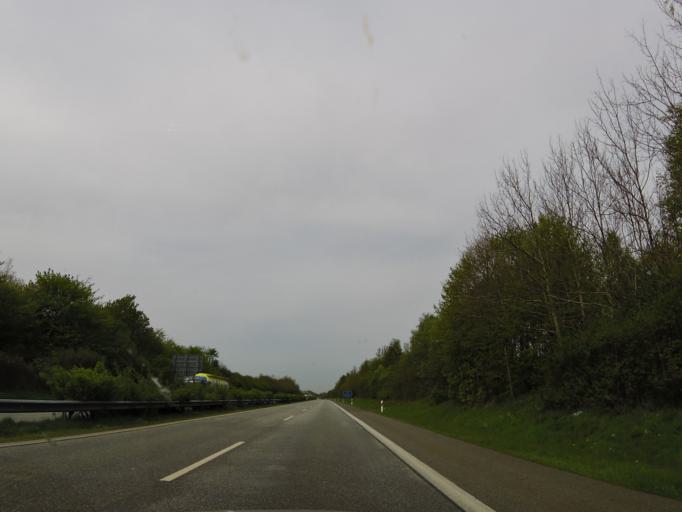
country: DE
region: Schleswig-Holstein
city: Besdorf
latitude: 54.0610
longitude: 9.3566
